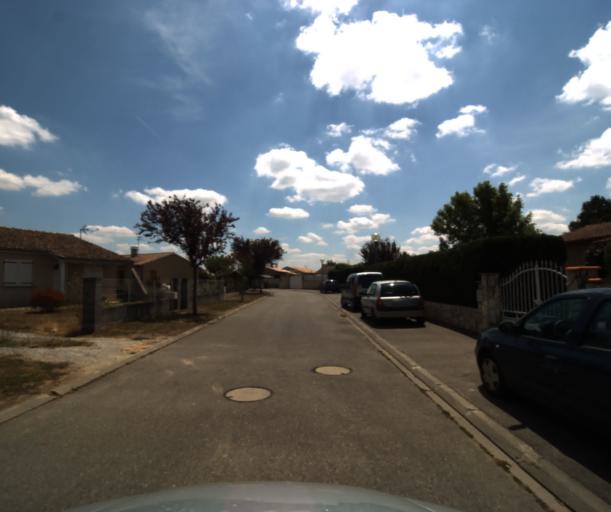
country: FR
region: Midi-Pyrenees
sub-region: Departement de la Haute-Garonne
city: Saint-Lys
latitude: 43.5043
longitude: 1.1740
